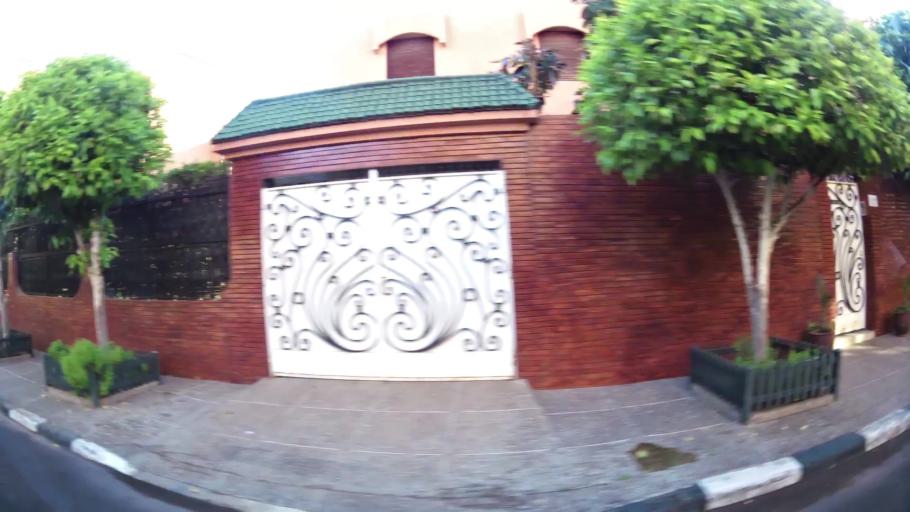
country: MA
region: Marrakech-Tensift-Al Haouz
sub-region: Marrakech
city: Marrakesh
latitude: 31.6494
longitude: -8.0185
